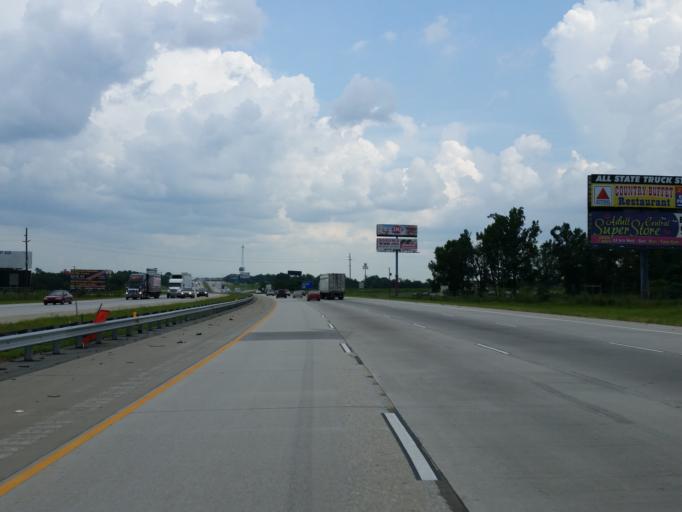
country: US
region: Georgia
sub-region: Dooly County
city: Unadilla
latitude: 32.2559
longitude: -83.7482
